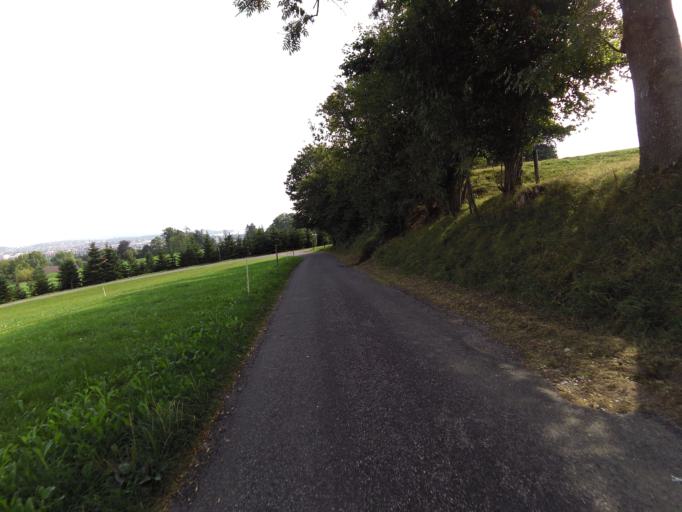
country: CH
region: Thurgau
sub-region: Kreuzlingen District
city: Tagerwilen
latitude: 47.6430
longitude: 9.1466
